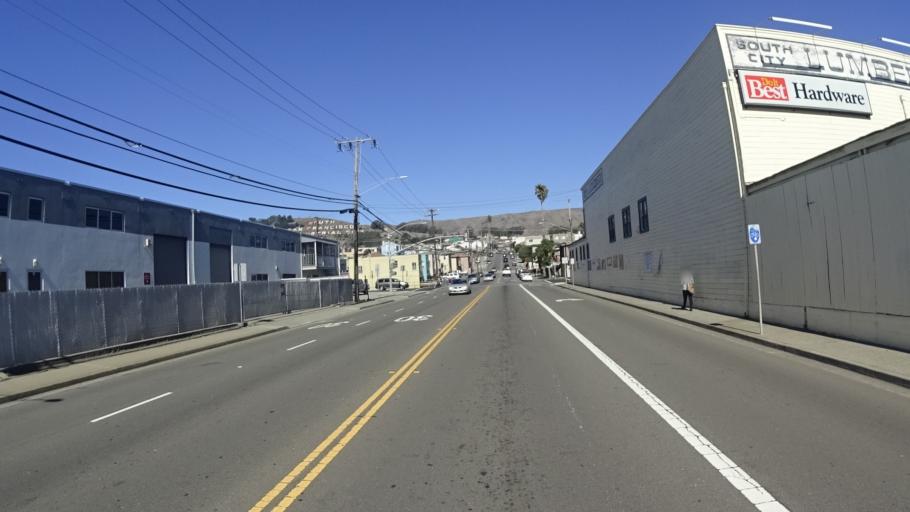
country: US
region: California
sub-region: San Mateo County
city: South San Francisco
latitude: 37.6529
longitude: -122.4173
